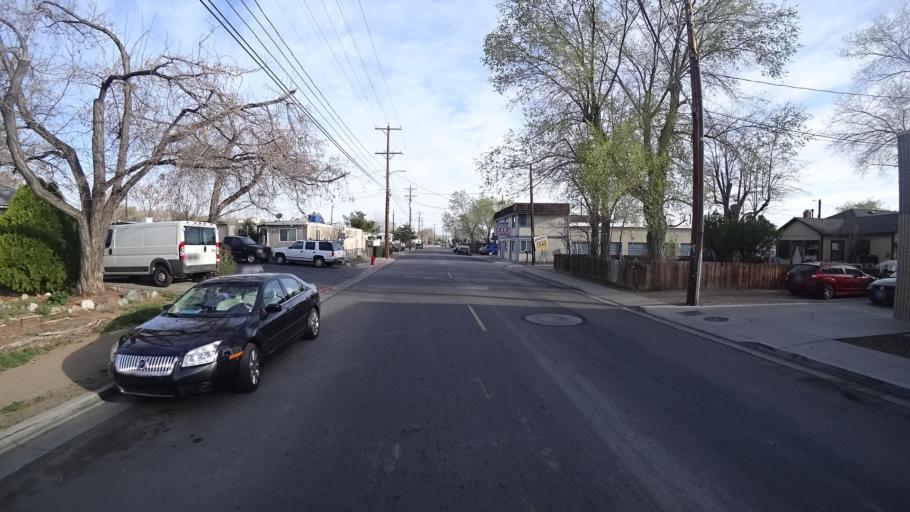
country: US
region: Nevada
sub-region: Washoe County
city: Reno
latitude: 39.4970
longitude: -119.7959
